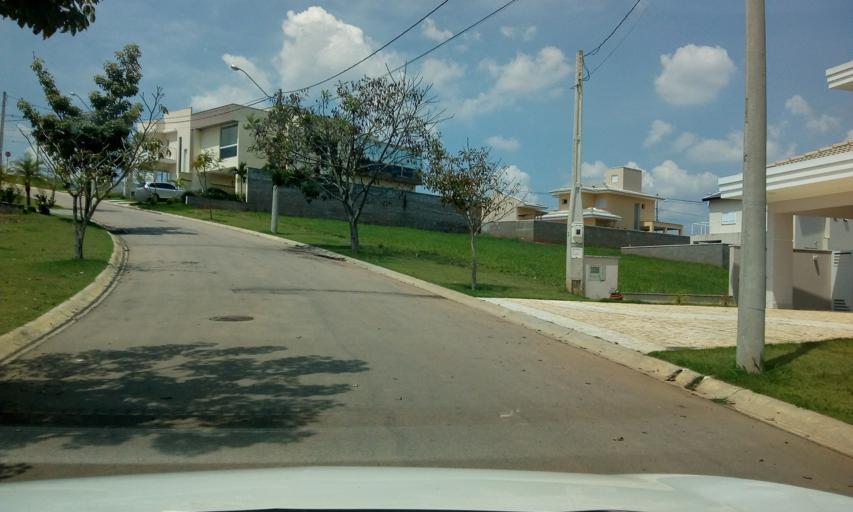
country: BR
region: Sao Paulo
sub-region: Itupeva
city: Itupeva
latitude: -23.1336
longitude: -47.0510
